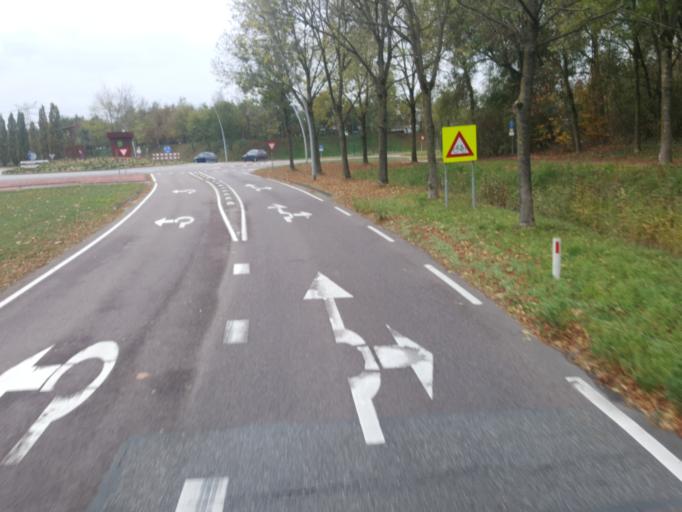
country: NL
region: North Brabant
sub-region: Gemeente Nuenen, Gerwen en Nederwetten
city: Nuenen
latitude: 51.4542
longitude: 5.5519
